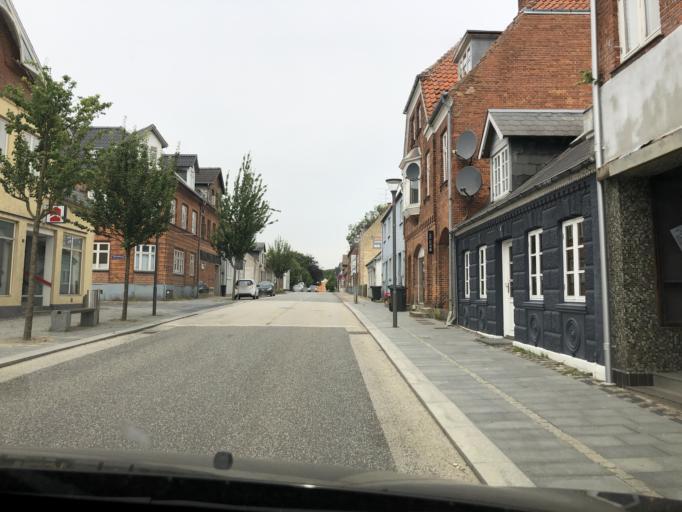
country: DK
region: South Denmark
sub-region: Assens Kommune
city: Glamsbjerg
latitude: 55.2791
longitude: 10.1044
